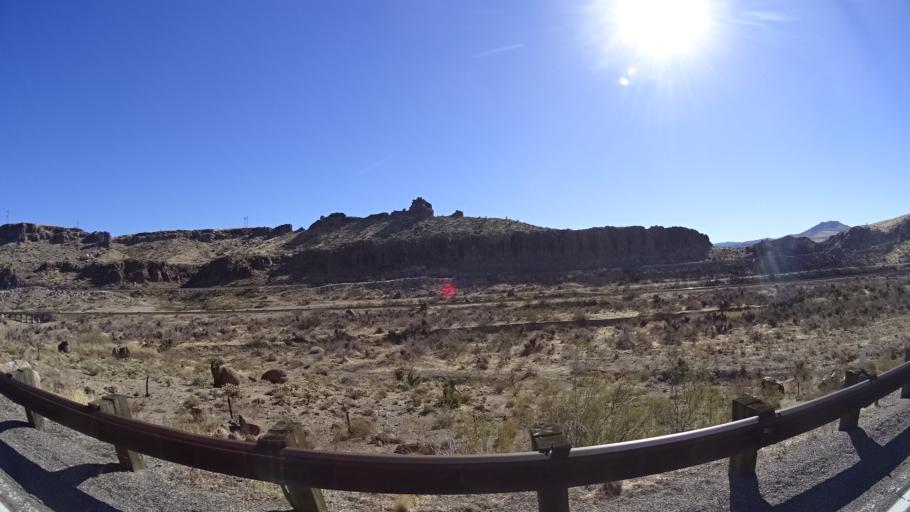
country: US
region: Arizona
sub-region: Mohave County
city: Kingman
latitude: 35.1684
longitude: -114.0612
